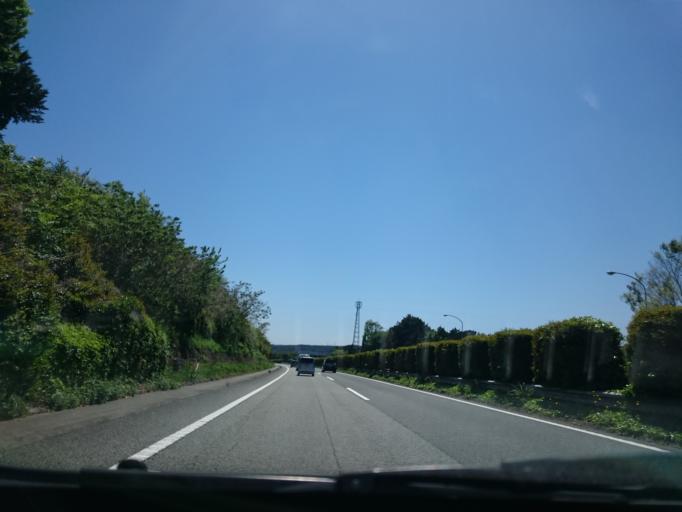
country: JP
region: Shizuoka
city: Gotemba
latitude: 35.2162
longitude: 138.9058
